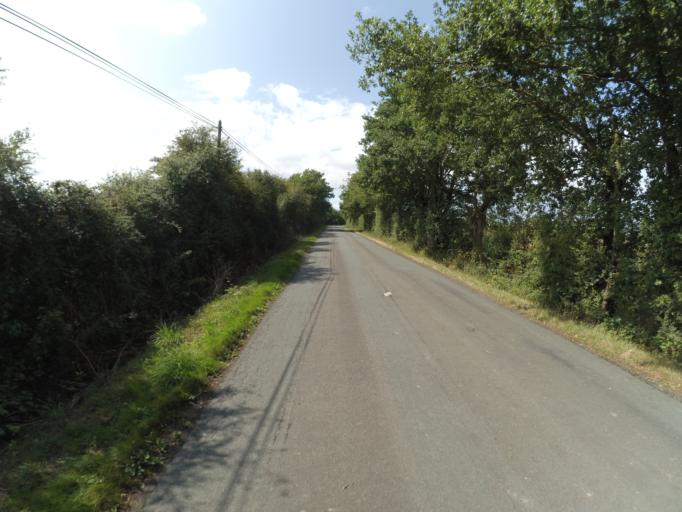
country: FR
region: Pays de la Loire
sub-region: Departement de la Vendee
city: La Bruffiere
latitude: 47.0221
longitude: -1.2225
